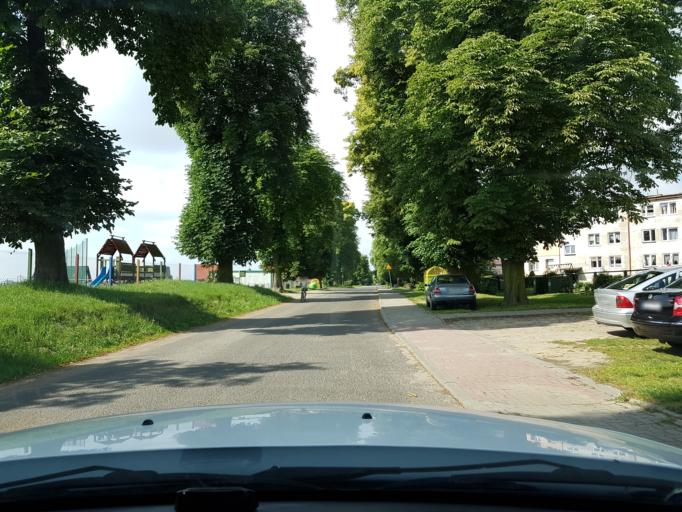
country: PL
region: West Pomeranian Voivodeship
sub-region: Powiat gryfinski
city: Banie
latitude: 53.1275
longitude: 14.6081
